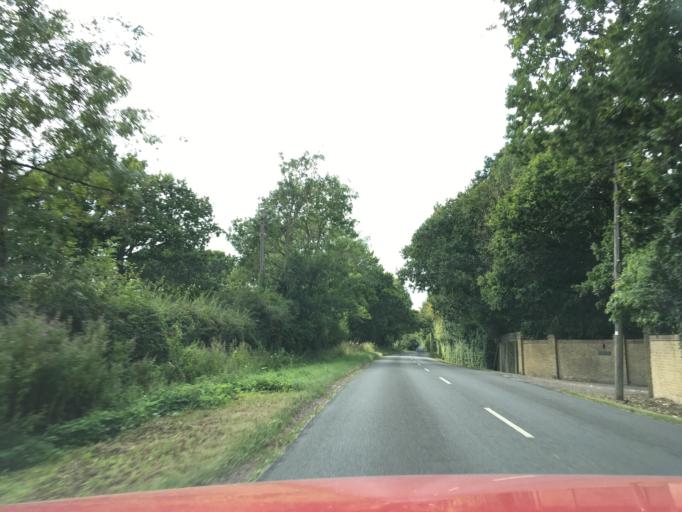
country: GB
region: England
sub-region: Kent
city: Tenterden
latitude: 51.0599
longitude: 0.7226
